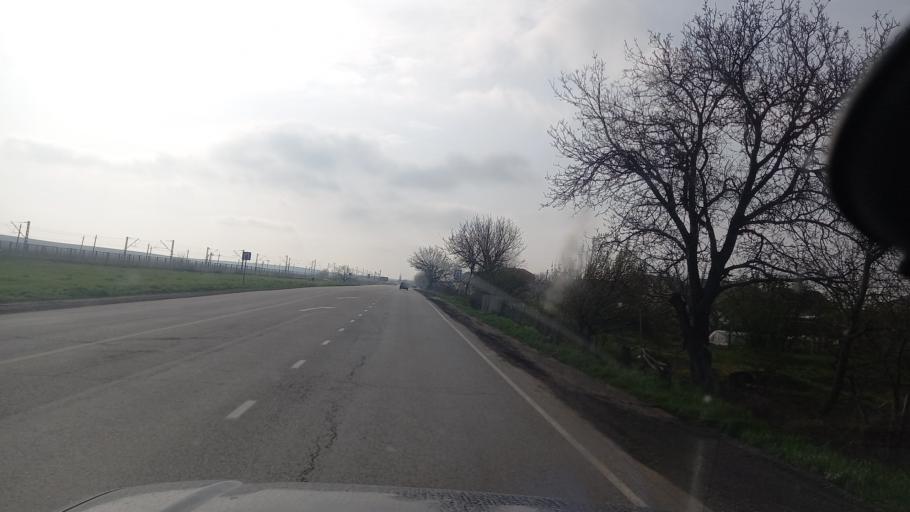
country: RU
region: Krasnodarskiy
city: Varenikovskaya
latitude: 45.1121
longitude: 37.6332
